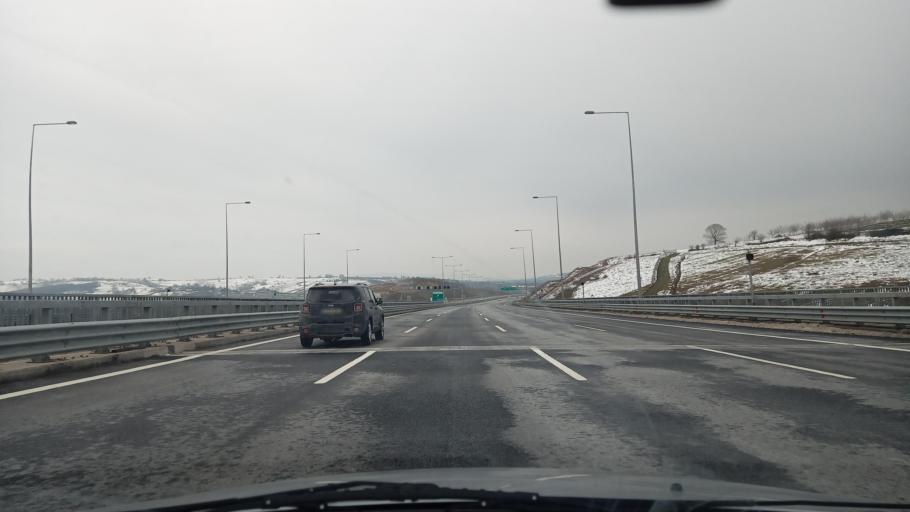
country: TR
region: Kocaeli
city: Akmese
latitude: 40.8415
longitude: 30.2090
